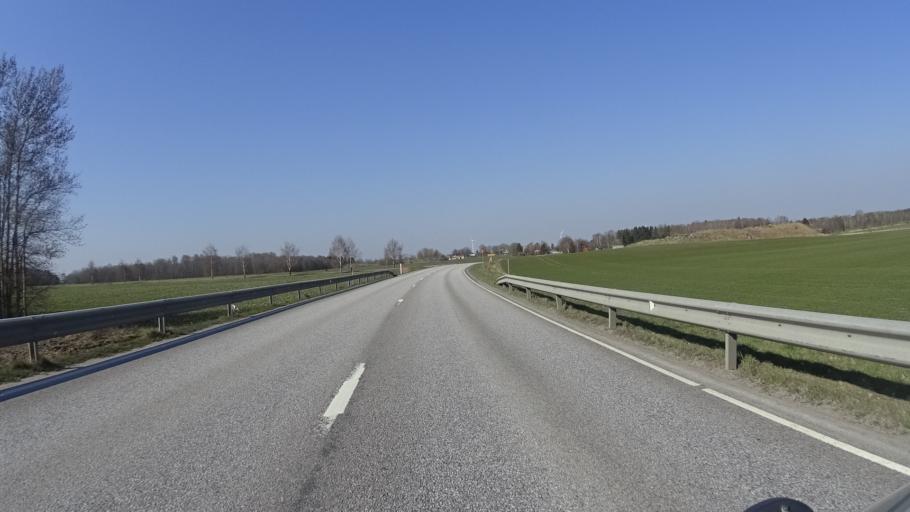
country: SE
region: OEstergoetland
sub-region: Mjolby Kommun
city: Mantorp
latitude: 58.3767
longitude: 15.2697
